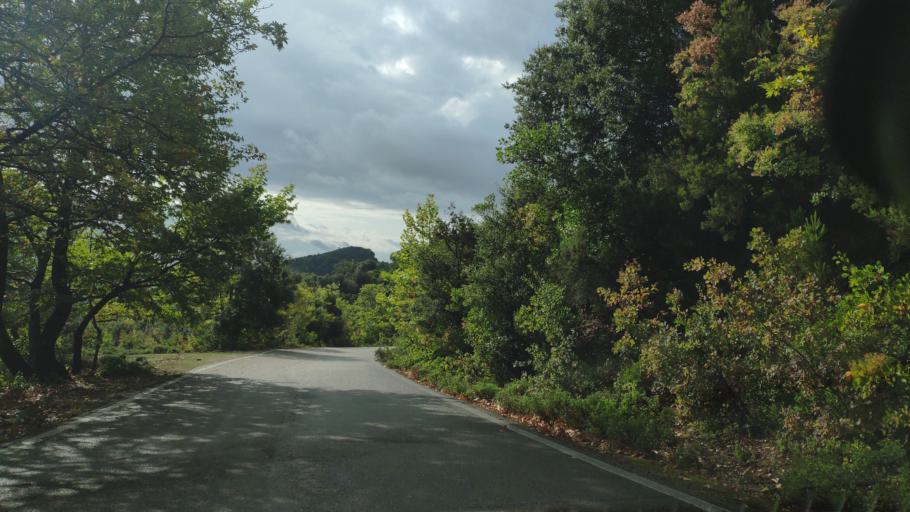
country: GR
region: West Greece
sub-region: Nomos Aitolias kai Akarnanias
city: Sardinia
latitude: 38.8608
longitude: 21.3038
